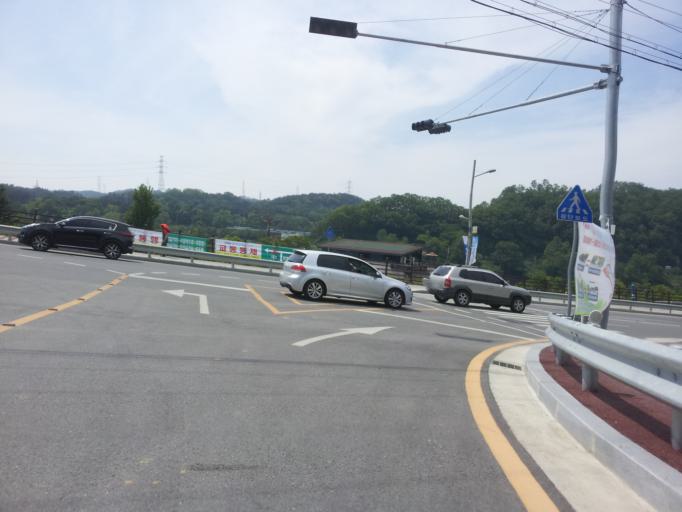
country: KR
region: Daejeon
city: Sintansin
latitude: 36.4590
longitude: 127.4657
